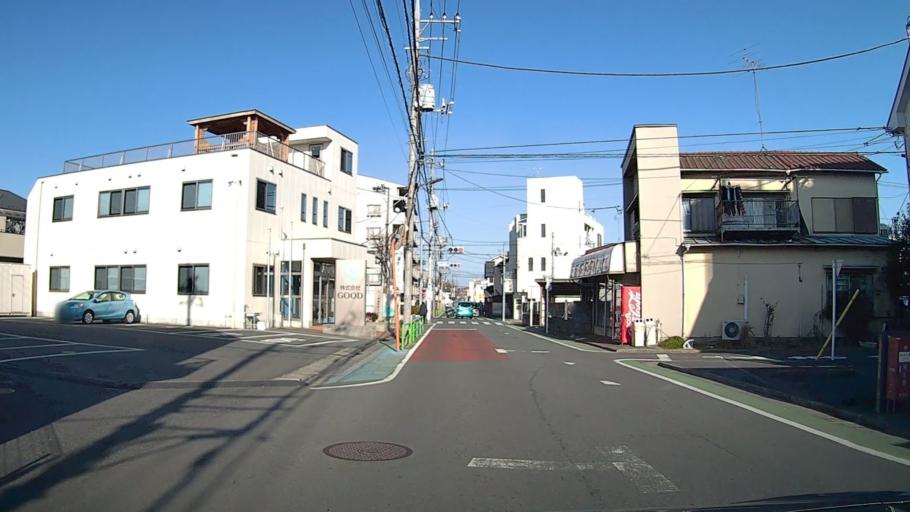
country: JP
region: Saitama
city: Asaka
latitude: 35.7613
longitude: 139.5768
